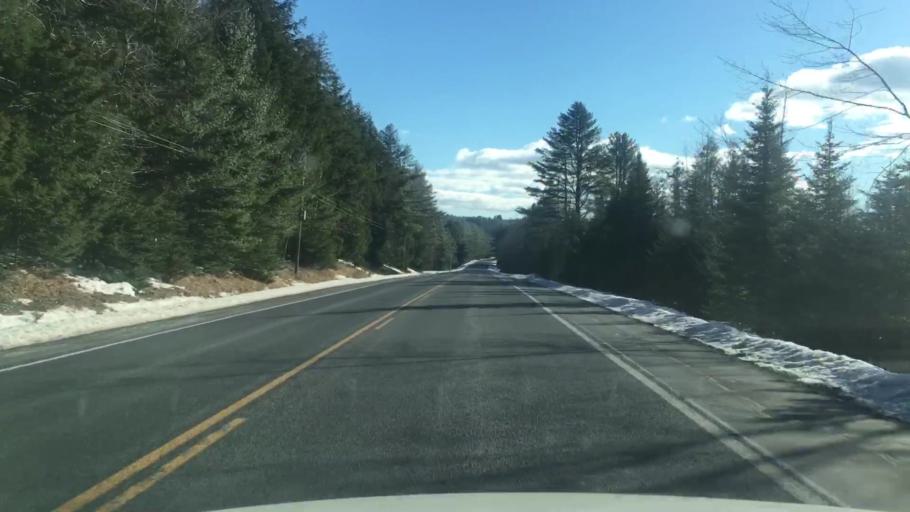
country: US
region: Maine
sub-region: Somerset County
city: Madison
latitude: 44.9105
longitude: -69.8196
